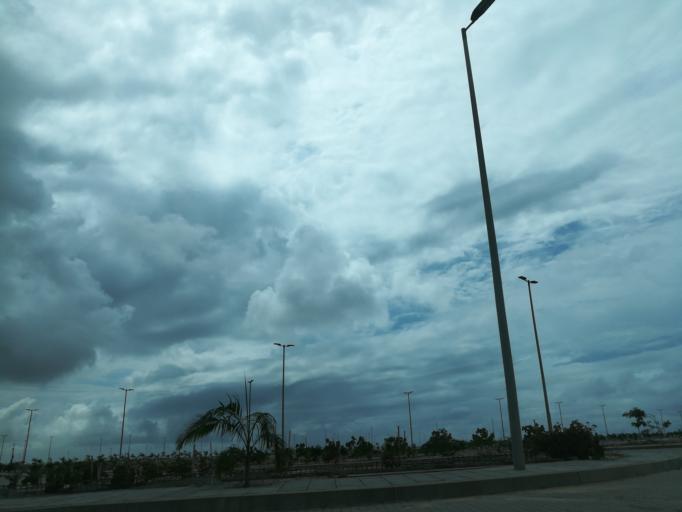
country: NG
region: Lagos
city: Lagos
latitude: 6.4161
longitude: 3.4122
